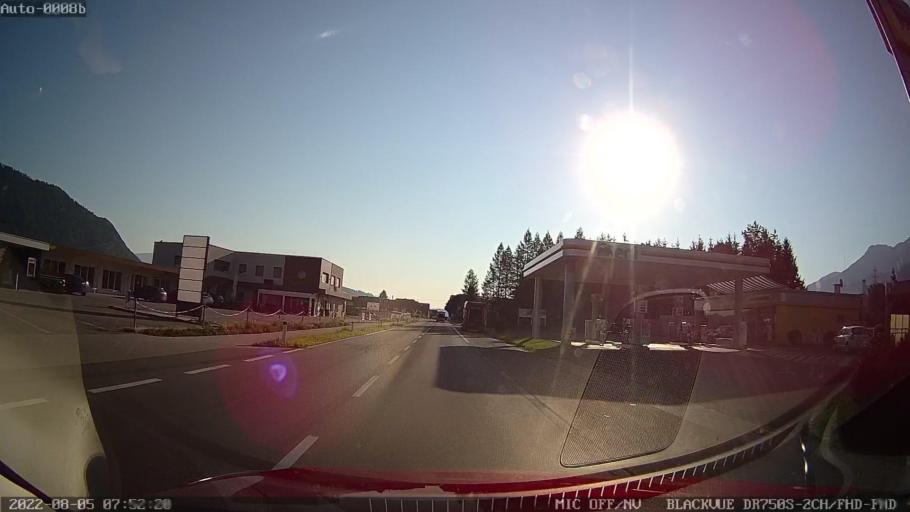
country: AT
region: Carinthia
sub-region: Politischer Bezirk Villach Land
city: Finkenstein am Faaker See
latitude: 46.5575
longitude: 13.7908
